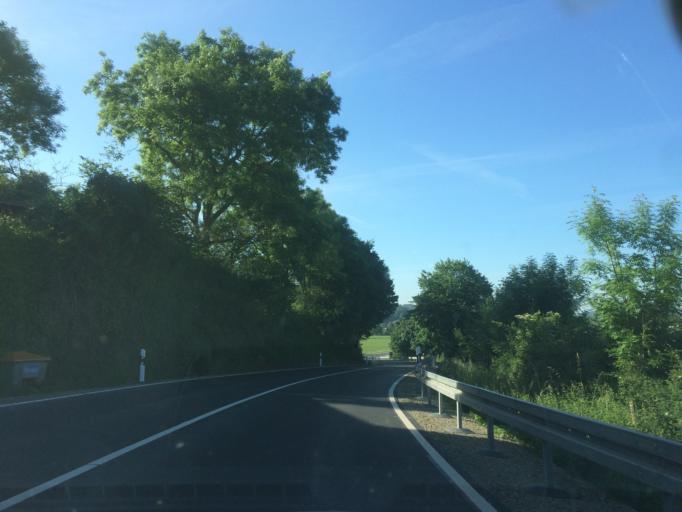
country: DE
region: Hesse
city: Trendelburg
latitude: 51.5867
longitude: 9.4148
